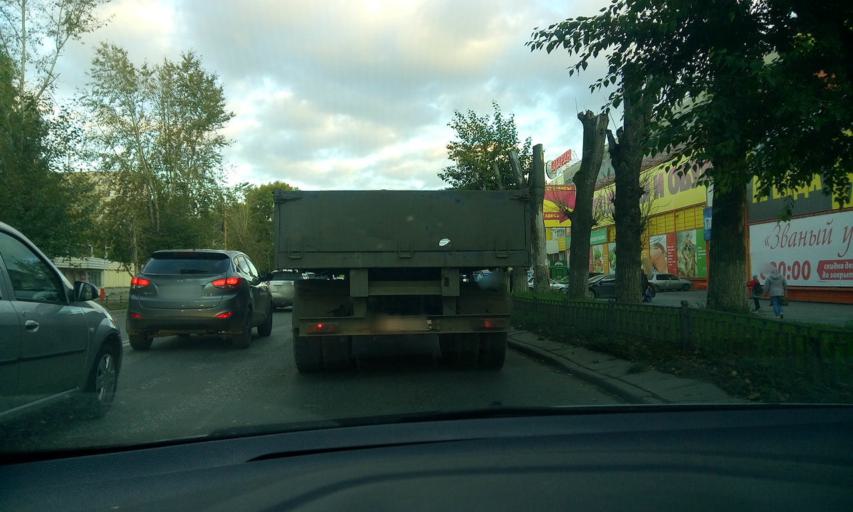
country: RU
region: Sverdlovsk
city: Yekaterinburg
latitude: 56.8242
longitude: 60.6492
